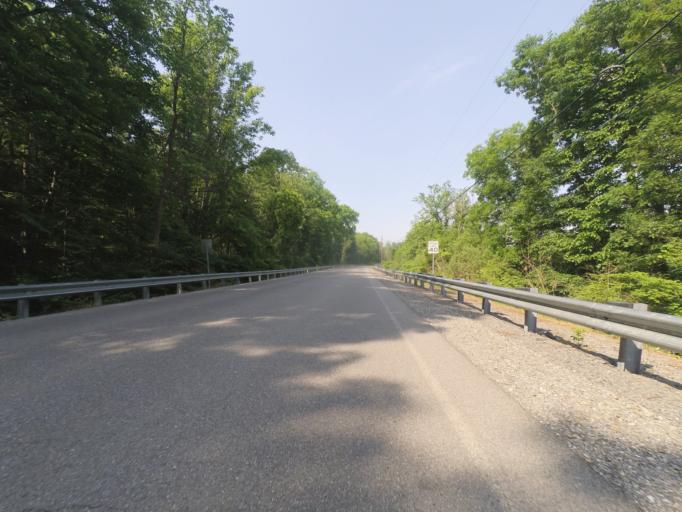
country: US
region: Pennsylvania
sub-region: Centre County
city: Zion
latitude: 40.9745
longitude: -77.7163
